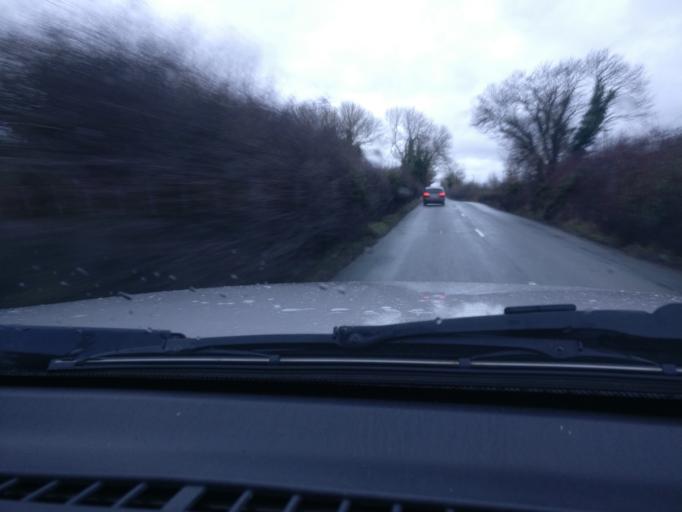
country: IE
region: Leinster
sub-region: An Mhi
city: Longwood
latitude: 53.4732
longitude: -6.9058
